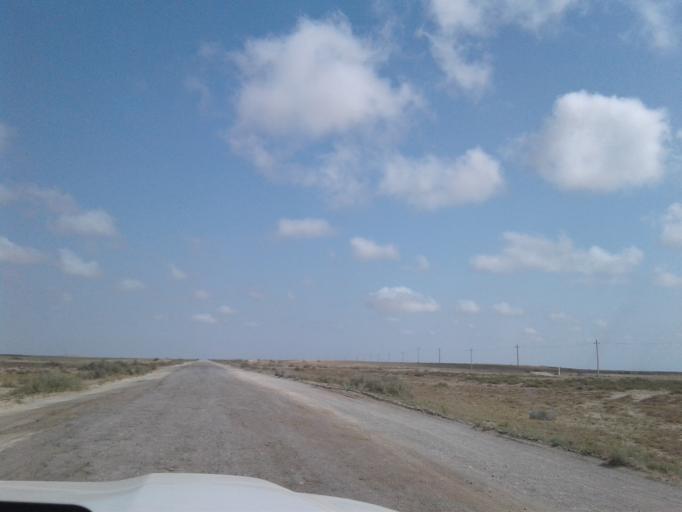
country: IR
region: Golestan
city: Gomishan
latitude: 37.6463
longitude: 53.9311
